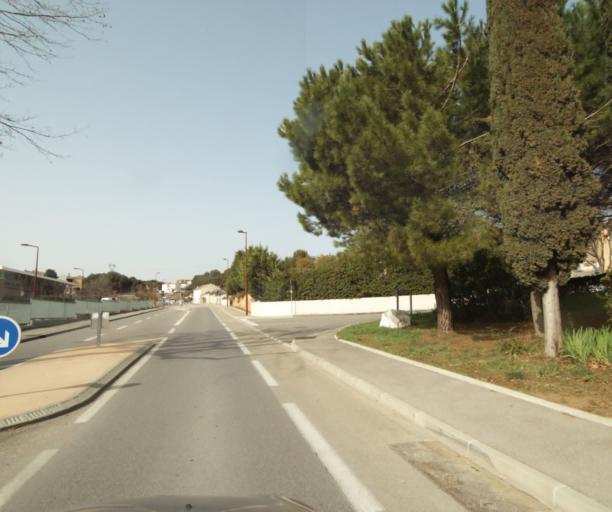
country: FR
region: Provence-Alpes-Cote d'Azur
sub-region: Departement des Bouches-du-Rhone
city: Septemes-les-Vallons
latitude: 43.3997
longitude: 5.3412
